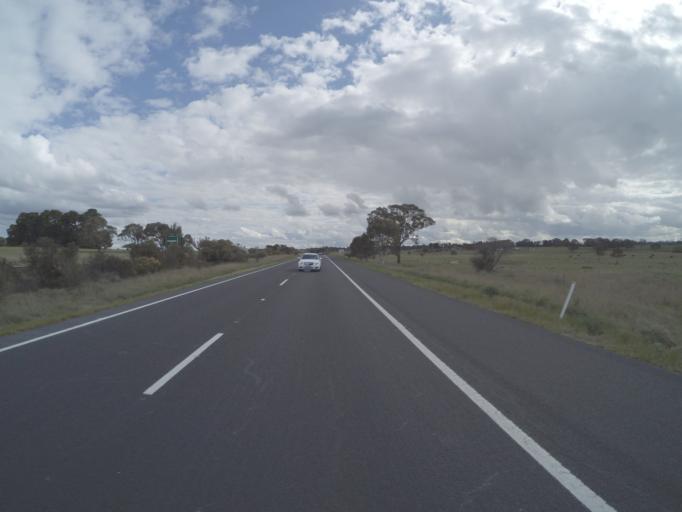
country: AU
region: New South Wales
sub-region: Goulburn Mulwaree
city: Goulburn
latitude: -34.7886
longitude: 149.6237
